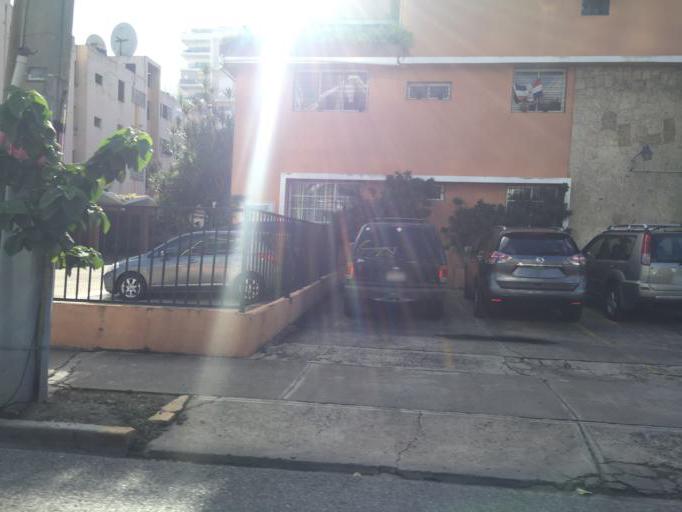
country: DO
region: Nacional
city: La Julia
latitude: 18.4798
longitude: -69.9383
